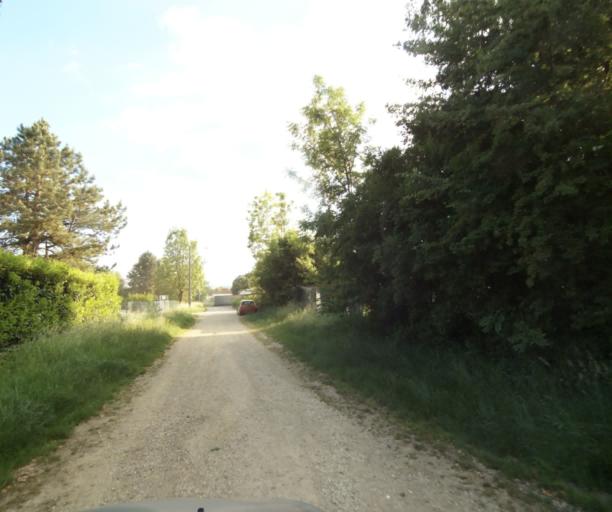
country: FR
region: Champagne-Ardenne
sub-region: Departement des Ardennes
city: Charleville-Mezieres
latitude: 49.7885
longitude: 4.7168
